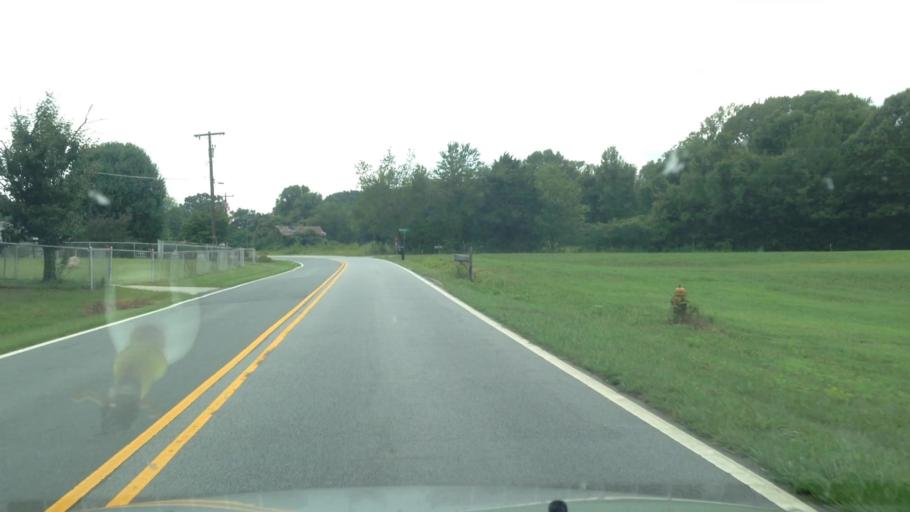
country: US
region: North Carolina
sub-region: Forsyth County
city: Walkertown
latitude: 36.1584
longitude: -80.1111
